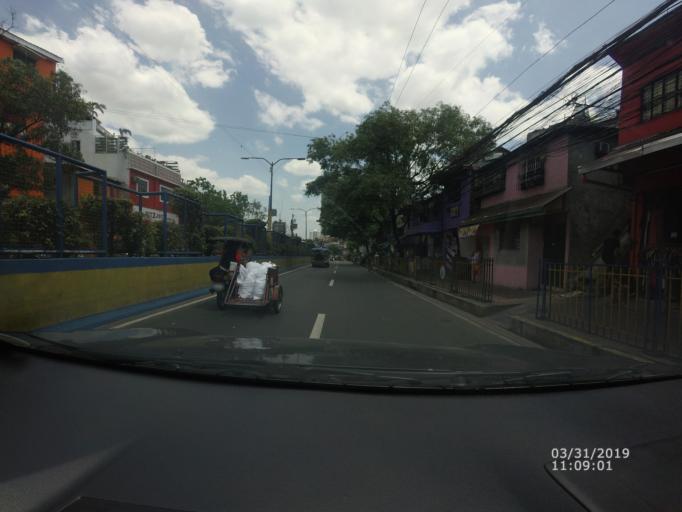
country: PH
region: Metro Manila
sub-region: Mandaluyong
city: Mandaluyong City
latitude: 14.5854
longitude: 121.0376
